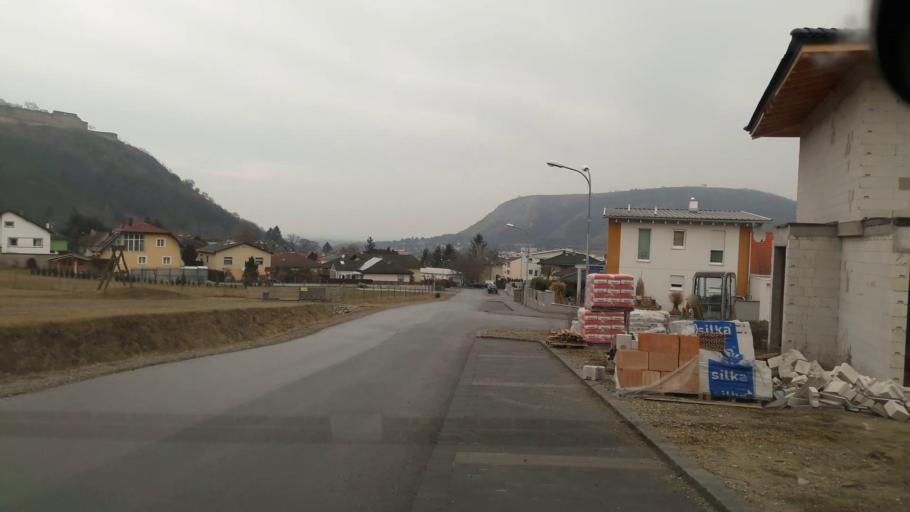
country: AT
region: Lower Austria
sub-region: Politischer Bezirk Bruck an der Leitha
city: Hainburg an der Donau
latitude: 48.1378
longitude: 16.9542
